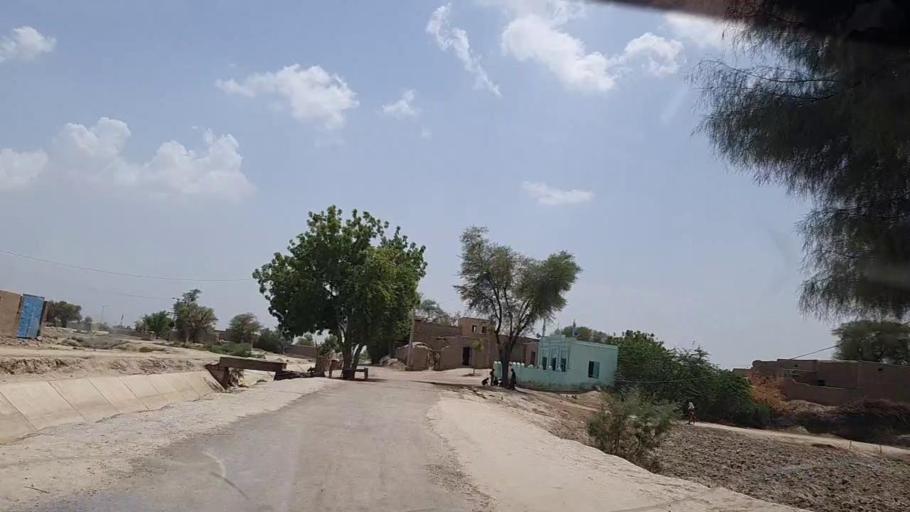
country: PK
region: Sindh
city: Bhan
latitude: 26.5394
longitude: 67.6337
